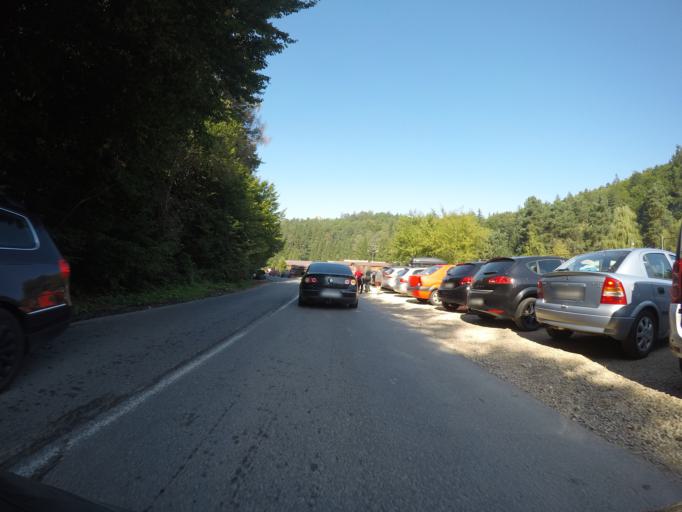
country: RO
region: Brasov
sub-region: Oras Rasnov
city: Rasnov
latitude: 45.5888
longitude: 25.4768
